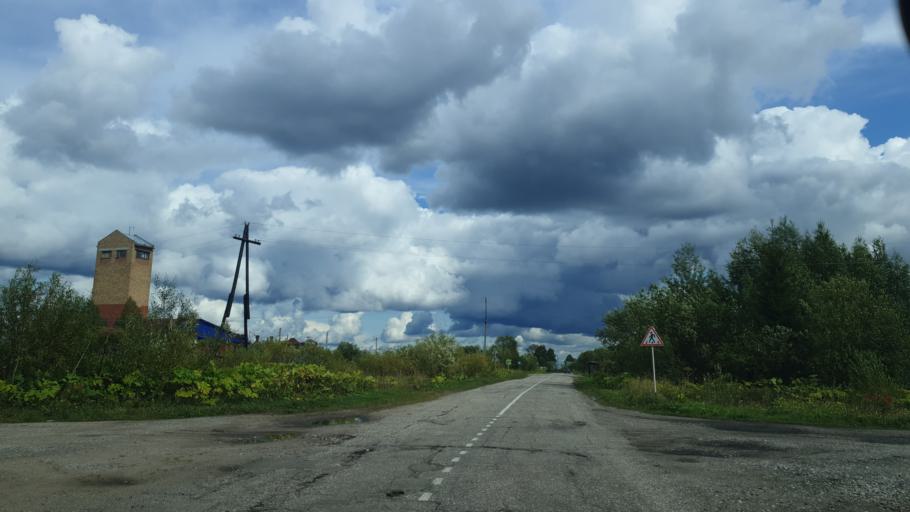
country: RU
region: Komi Republic
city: Aykino
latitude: 61.9518
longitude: 50.1726
